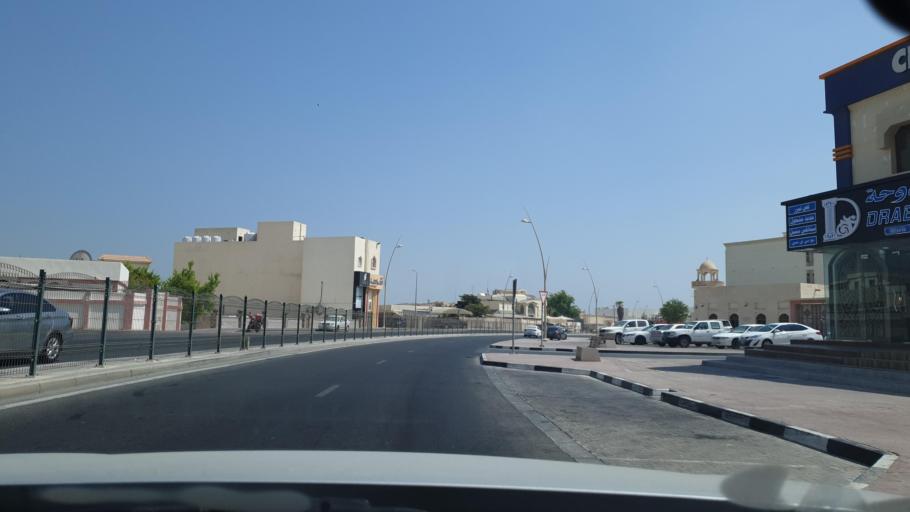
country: QA
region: Al Khawr
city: Al Khawr
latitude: 25.6840
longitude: 51.5106
